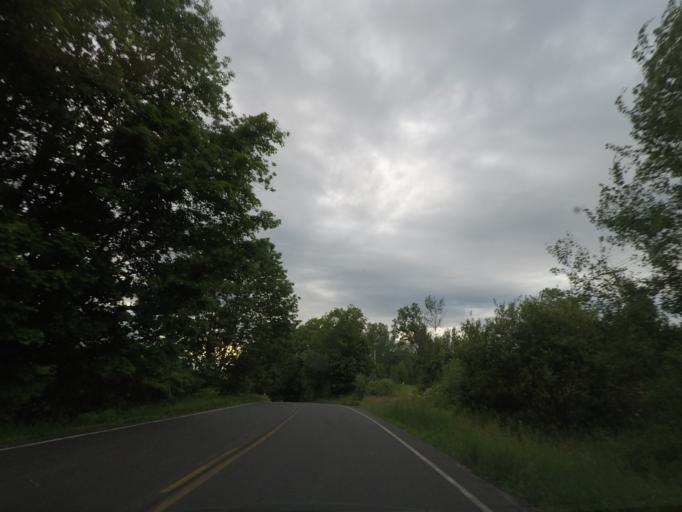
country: US
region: New York
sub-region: Dutchess County
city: Pine Plains
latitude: 41.9719
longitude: -73.5601
